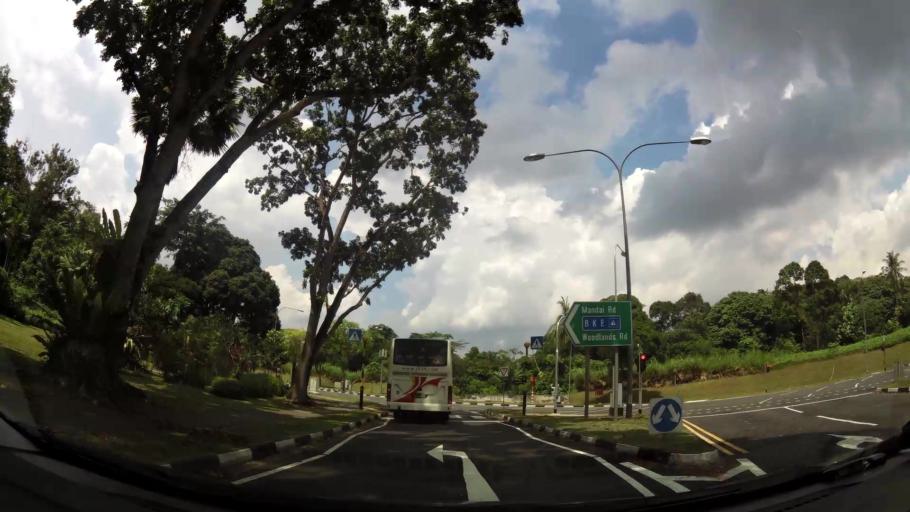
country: MY
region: Johor
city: Johor Bahru
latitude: 1.4105
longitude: 103.7786
